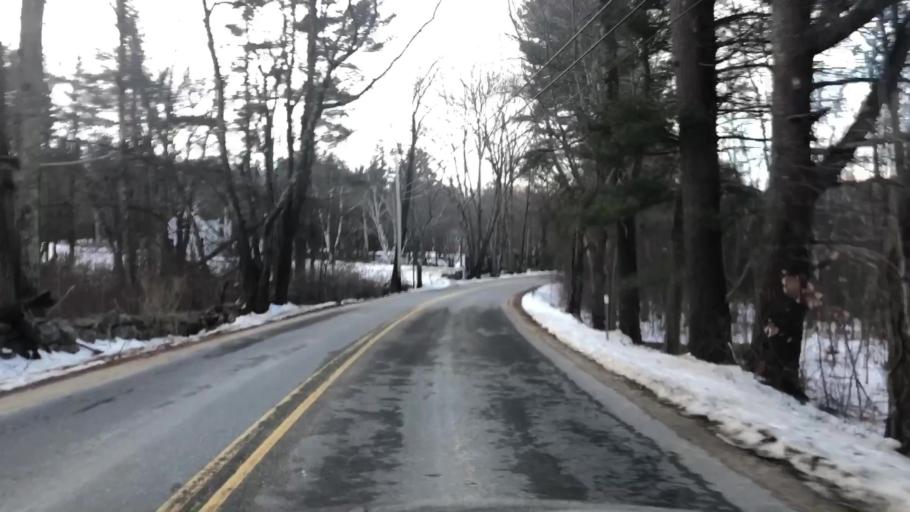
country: US
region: New Hampshire
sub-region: Hillsborough County
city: Milford
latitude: 42.8631
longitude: -71.6338
